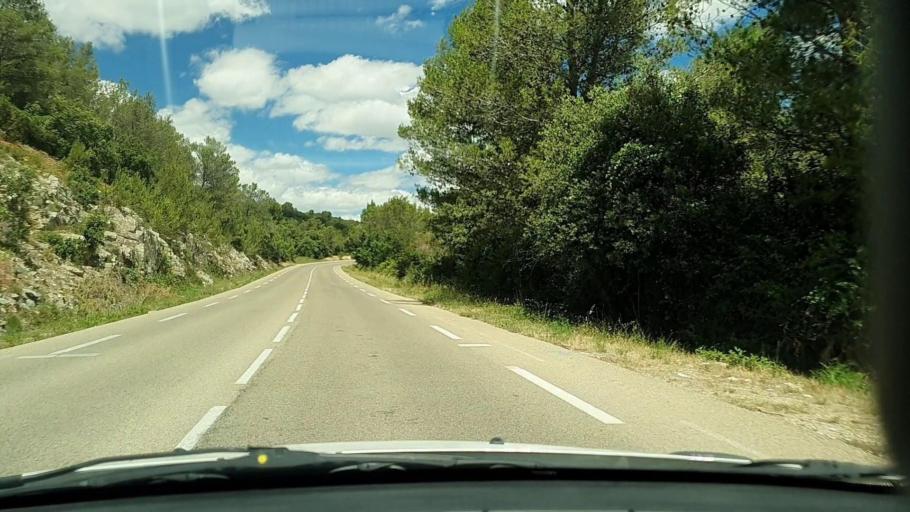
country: FR
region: Languedoc-Roussillon
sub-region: Departement du Gard
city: Poulx
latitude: 43.8821
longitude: 4.4172
